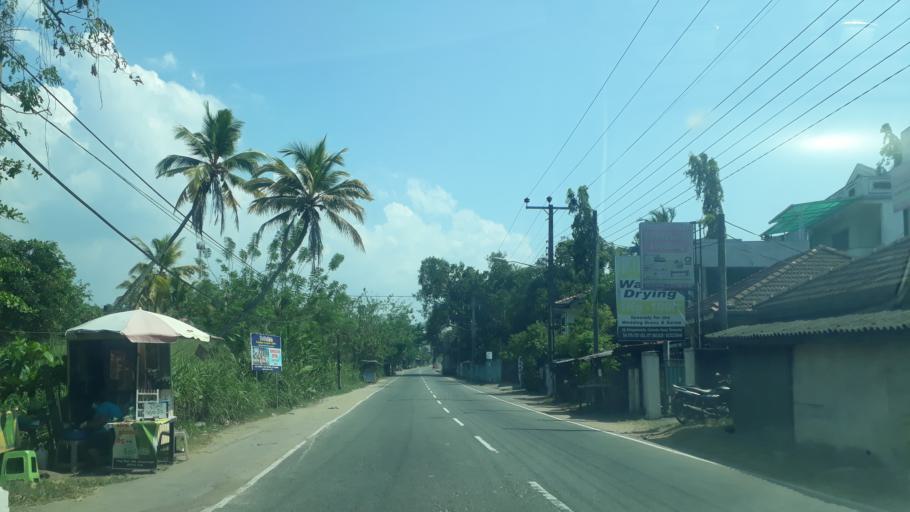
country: LK
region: Western
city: Gampaha
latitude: 7.0833
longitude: 80.0104
